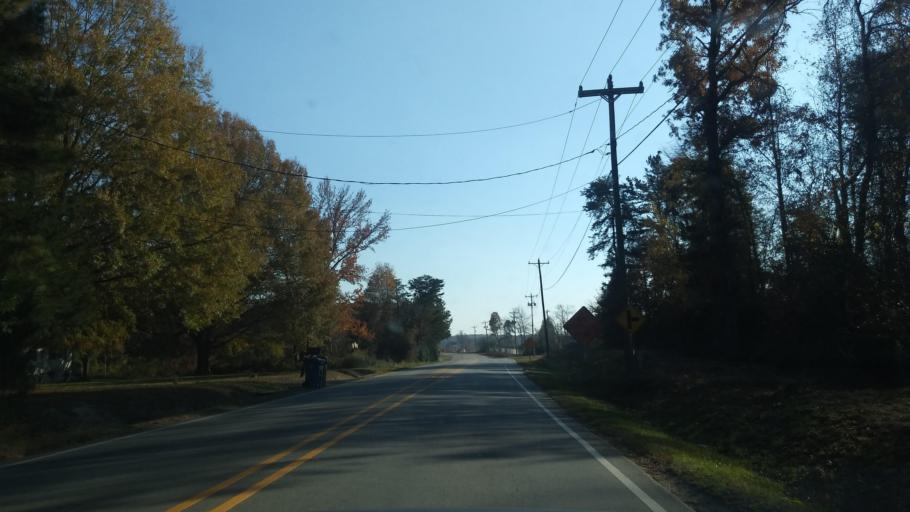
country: US
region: North Carolina
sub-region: Guilford County
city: McLeansville
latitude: 36.1938
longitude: -79.7063
